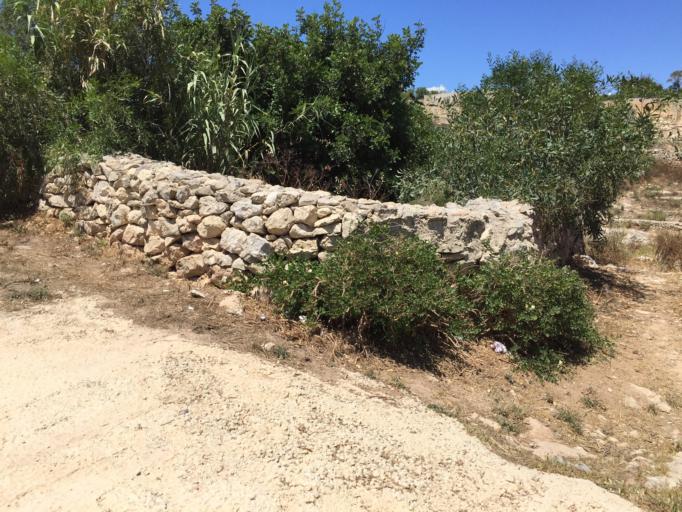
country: MT
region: Is-Swieqi
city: Swieqi
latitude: 35.9161
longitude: 14.4780
